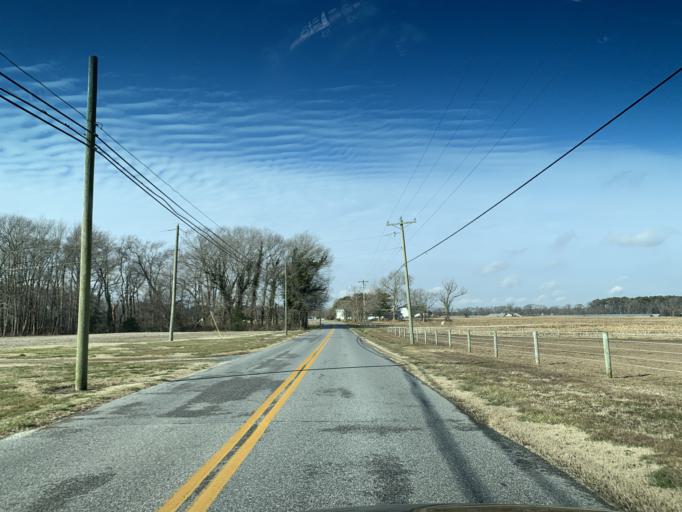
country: US
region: Maryland
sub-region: Worcester County
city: Ocean Pines
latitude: 38.4323
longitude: -75.1787
